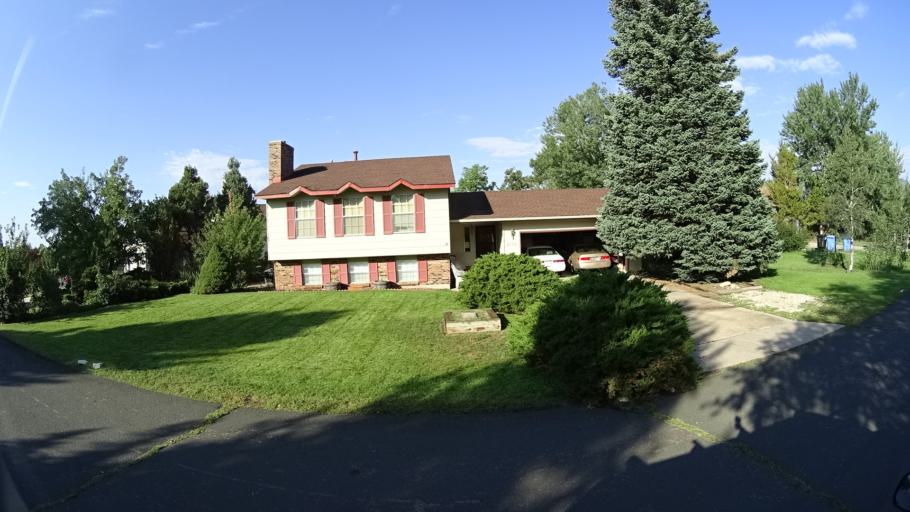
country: US
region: Colorado
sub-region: El Paso County
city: Air Force Academy
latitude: 38.9459
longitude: -104.7864
